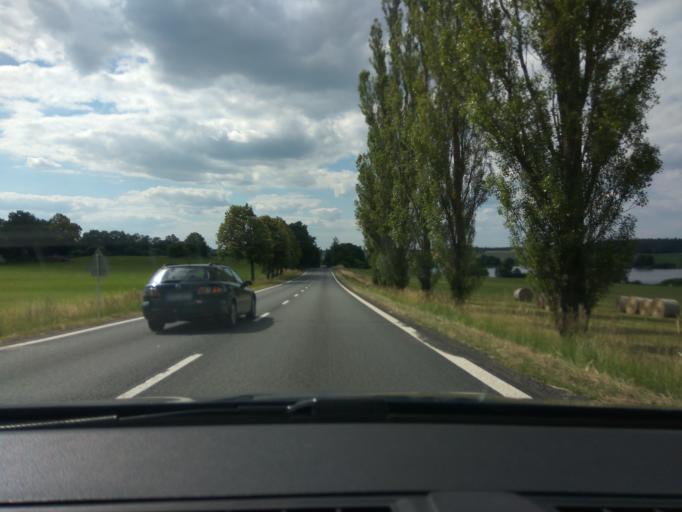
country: CZ
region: Jihocesky
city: Kovarov
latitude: 49.4914
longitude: 14.2380
